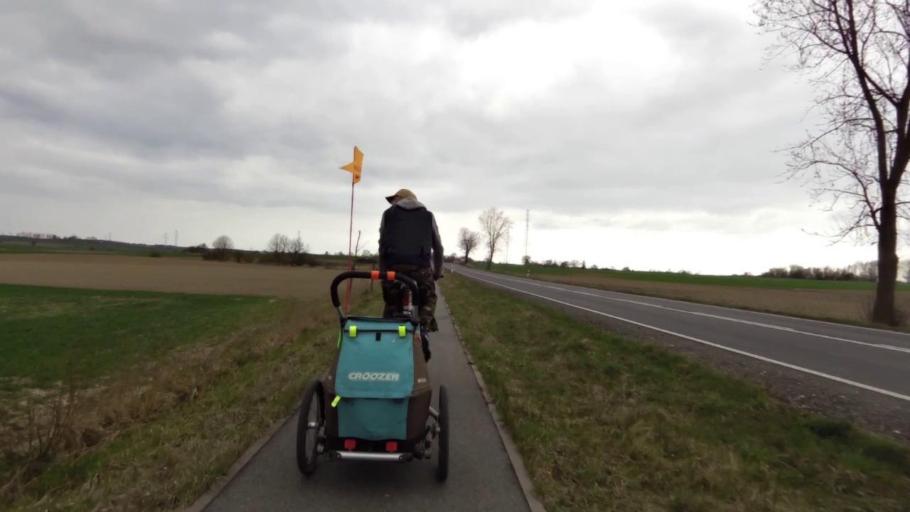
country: PL
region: West Pomeranian Voivodeship
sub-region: Powiat koszalinski
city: Sianow
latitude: 54.2935
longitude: 16.2935
